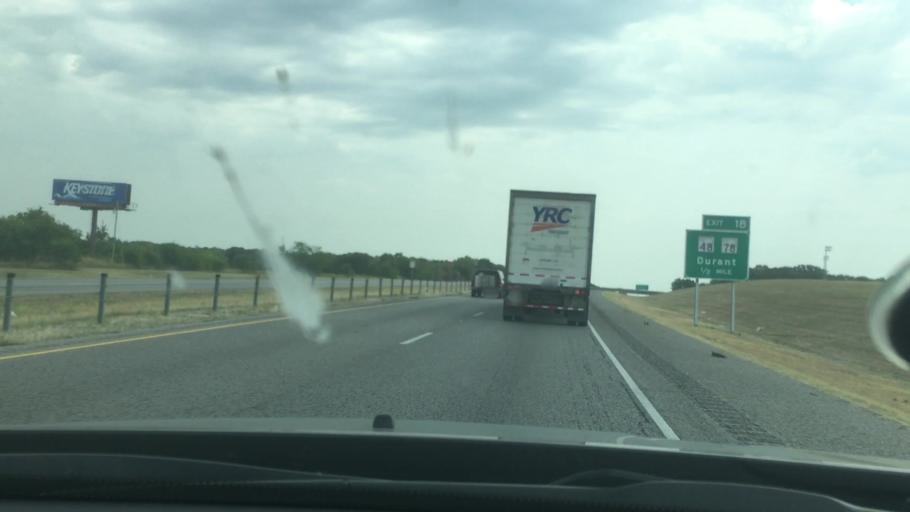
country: US
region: Oklahoma
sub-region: Bryan County
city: Durant
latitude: 34.0295
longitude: -96.3834
